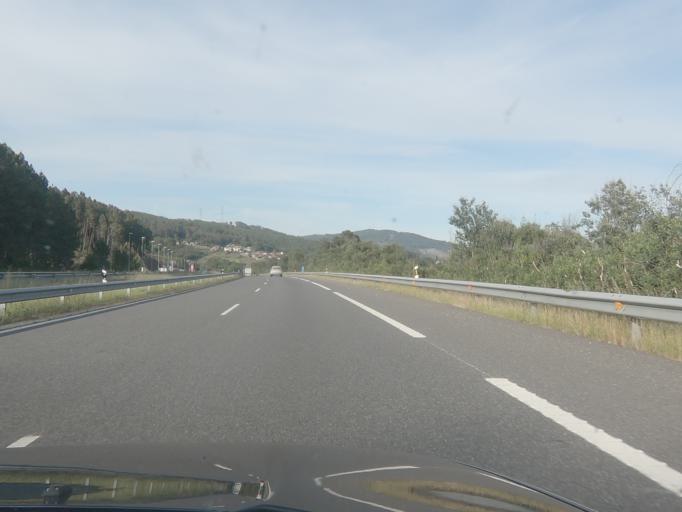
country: ES
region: Galicia
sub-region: Provincia de Ourense
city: Cenlle
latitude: 42.3100
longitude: -8.0977
